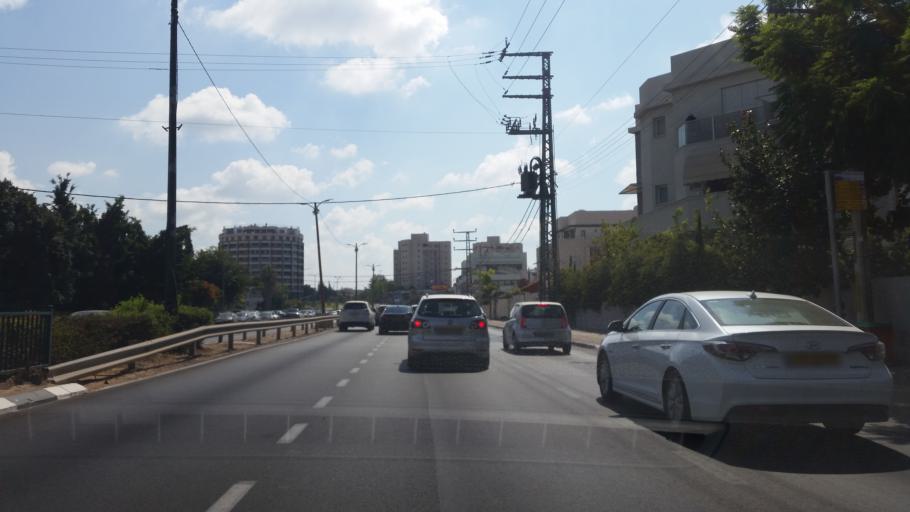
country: IL
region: Tel Aviv
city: Ramat HaSharon
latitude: 32.1257
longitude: 34.8258
